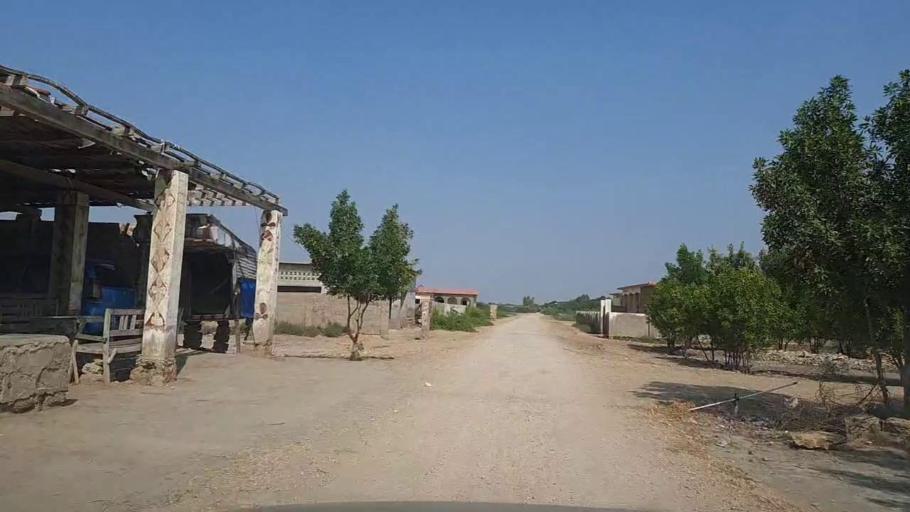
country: PK
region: Sindh
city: Thatta
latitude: 24.6141
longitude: 67.9580
